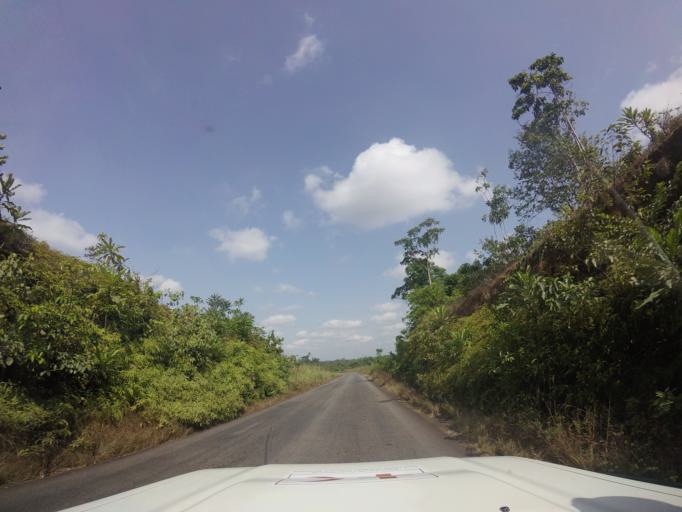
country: LR
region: Bomi
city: Tubmanburg
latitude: 6.7124
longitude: -10.9371
